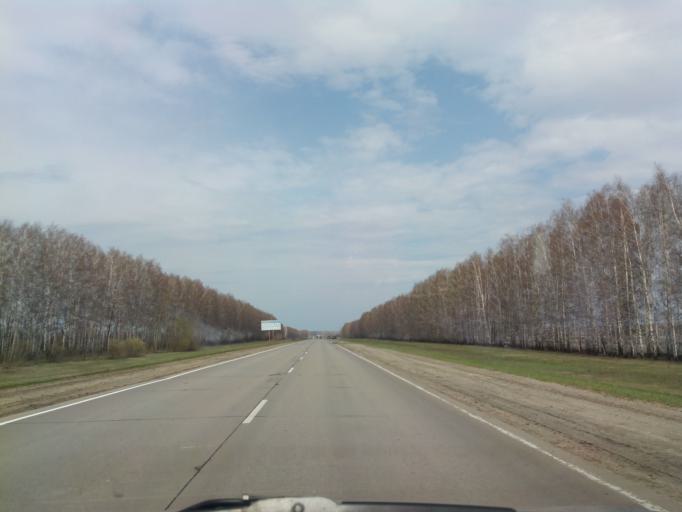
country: RU
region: Tambov
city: Zherdevka
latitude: 52.0646
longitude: 41.6640
